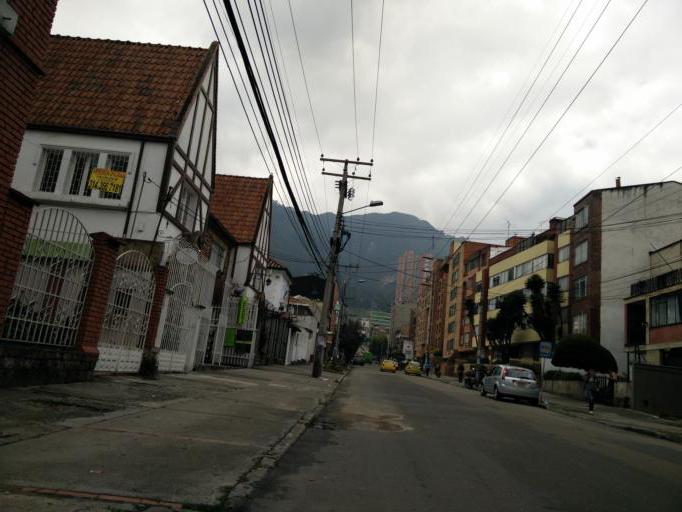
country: CO
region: Bogota D.C.
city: Barrio San Luis
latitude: 4.6491
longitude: -74.0587
